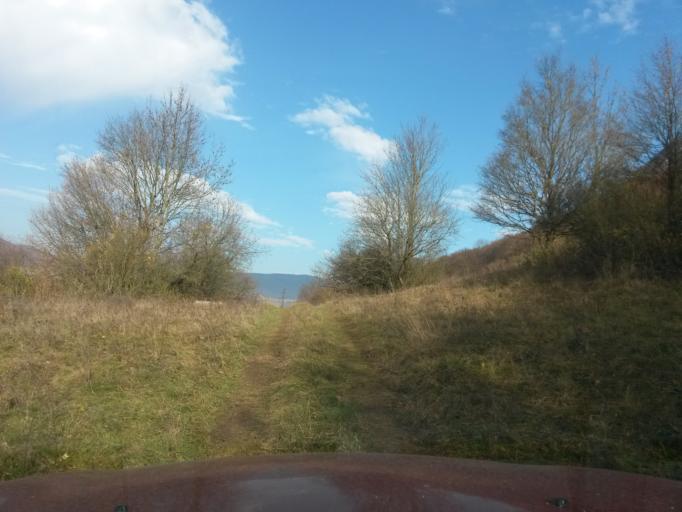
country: SK
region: Kosicky
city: Roznava
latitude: 48.5976
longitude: 20.4846
